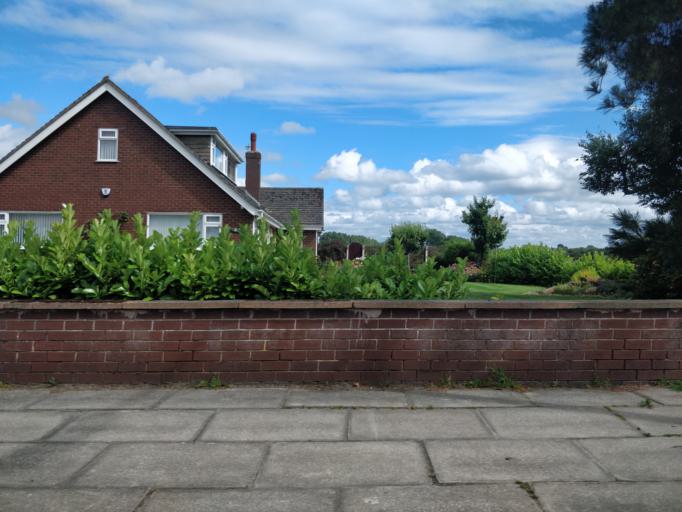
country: GB
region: England
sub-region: Lancashire
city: Banks
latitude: 53.6644
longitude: -2.9541
